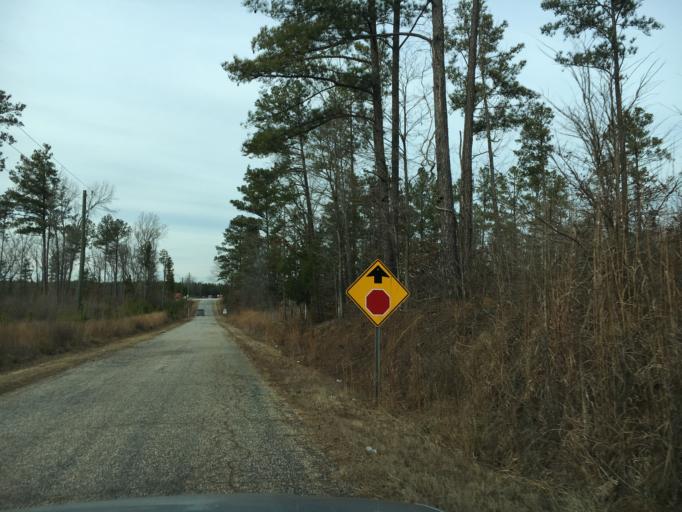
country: US
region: South Carolina
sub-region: Laurens County
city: Clinton
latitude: 34.5001
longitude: -81.8119
